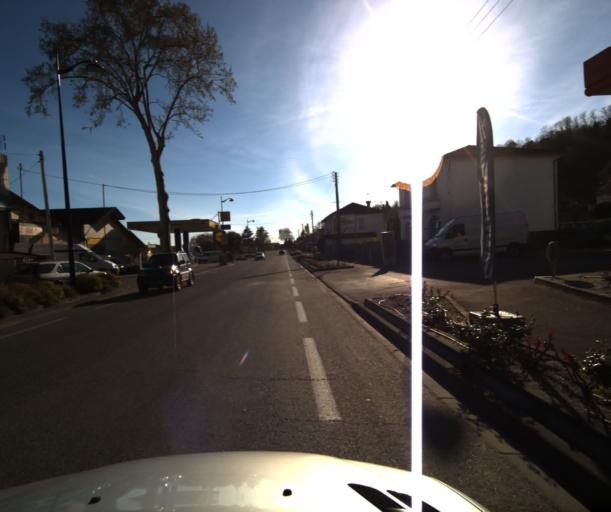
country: FR
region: Midi-Pyrenees
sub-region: Departement du Tarn-et-Garonne
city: Moissac
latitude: 44.1099
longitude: 1.1027
